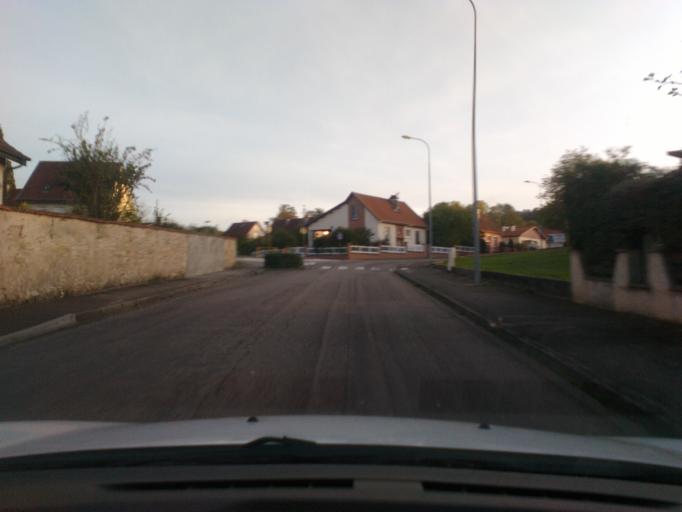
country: FR
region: Lorraine
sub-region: Departement des Vosges
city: Charmes
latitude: 48.3727
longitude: 6.2864
